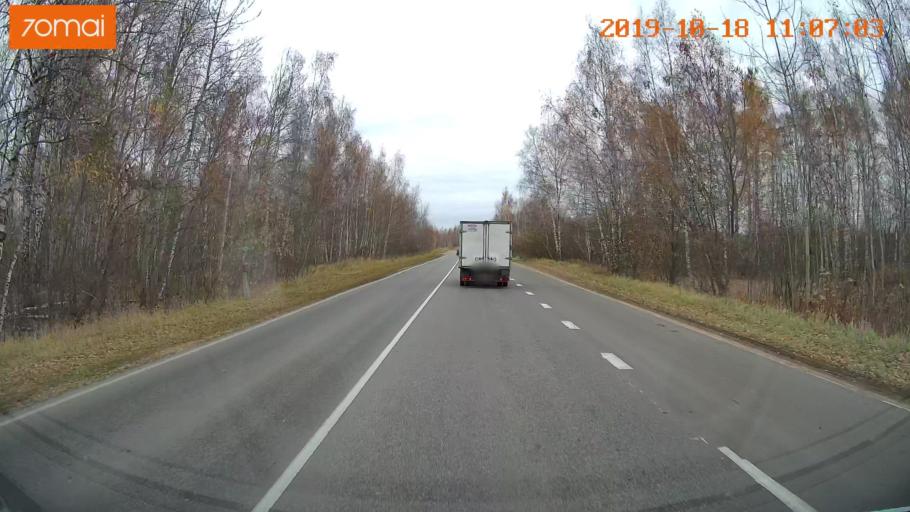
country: RU
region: Tula
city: Kimovsk
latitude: 53.9241
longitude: 38.5349
